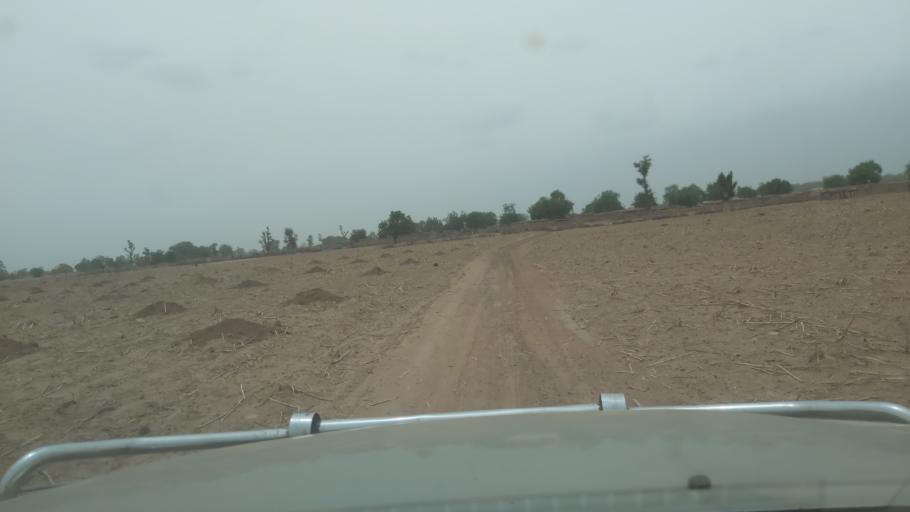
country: ML
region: Koulikoro
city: Banamba
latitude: 13.3762
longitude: -7.2258
